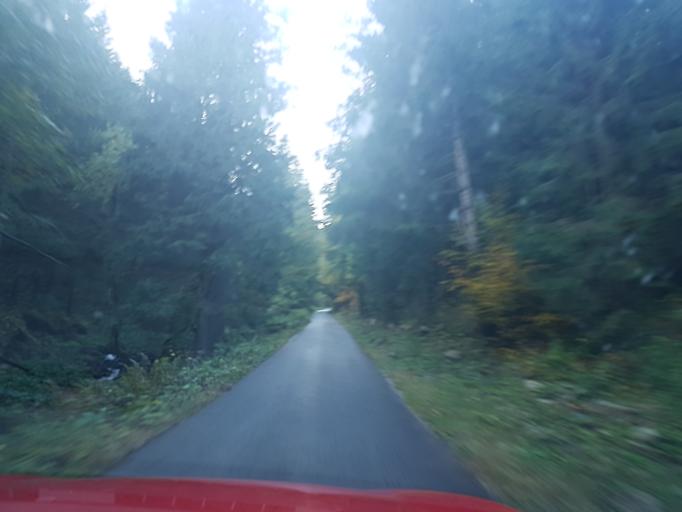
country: SK
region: Zilinsky
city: Ruzomberok
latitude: 48.9967
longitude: 19.2327
